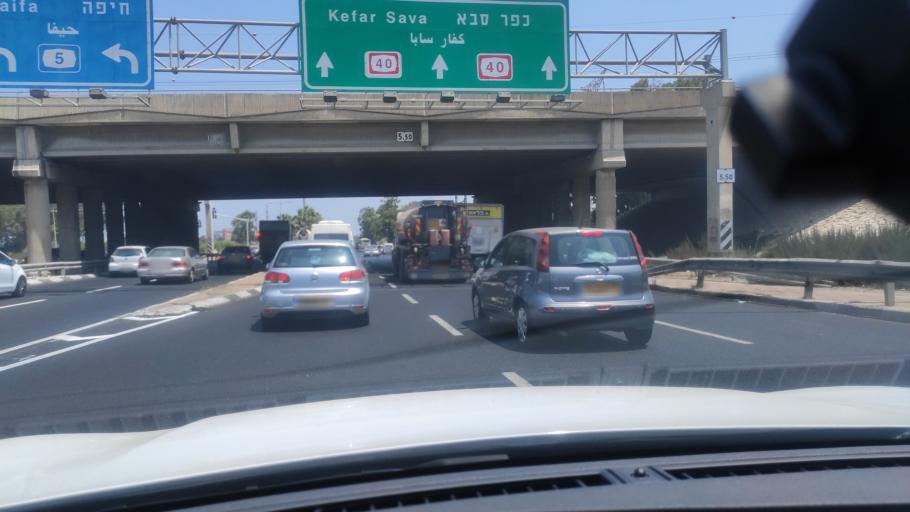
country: IL
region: Central District
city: Petah Tiqwa
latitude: 32.1205
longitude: 34.9036
